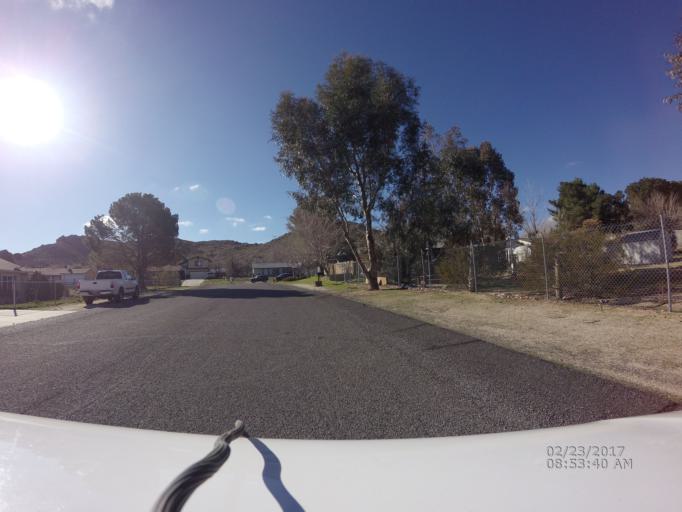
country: US
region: California
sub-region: Los Angeles County
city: Lake Los Angeles
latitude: 34.6091
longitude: -117.8184
